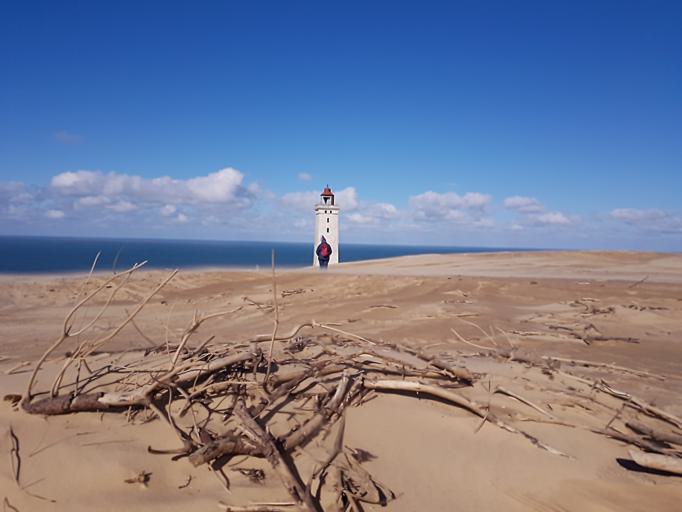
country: DK
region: North Denmark
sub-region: Hjorring Kommune
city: Vra
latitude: 57.4477
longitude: 9.7745
